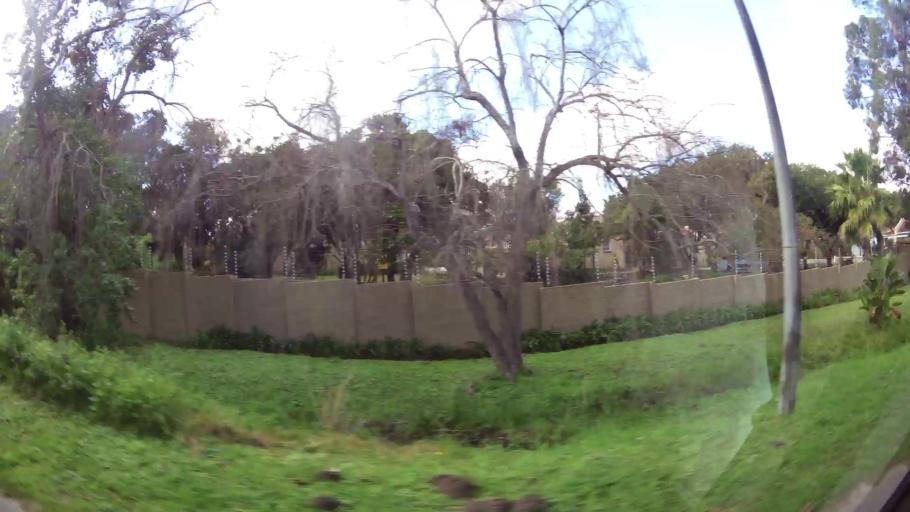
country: ZA
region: Western Cape
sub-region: Eden District Municipality
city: Knysna
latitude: -34.0393
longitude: 23.0724
